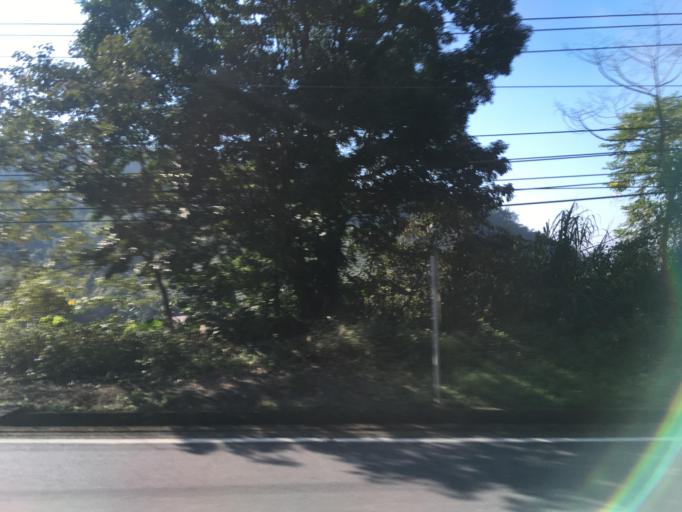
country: TW
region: Taiwan
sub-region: Chiayi
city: Jiayi Shi
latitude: 23.4224
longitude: 120.6433
